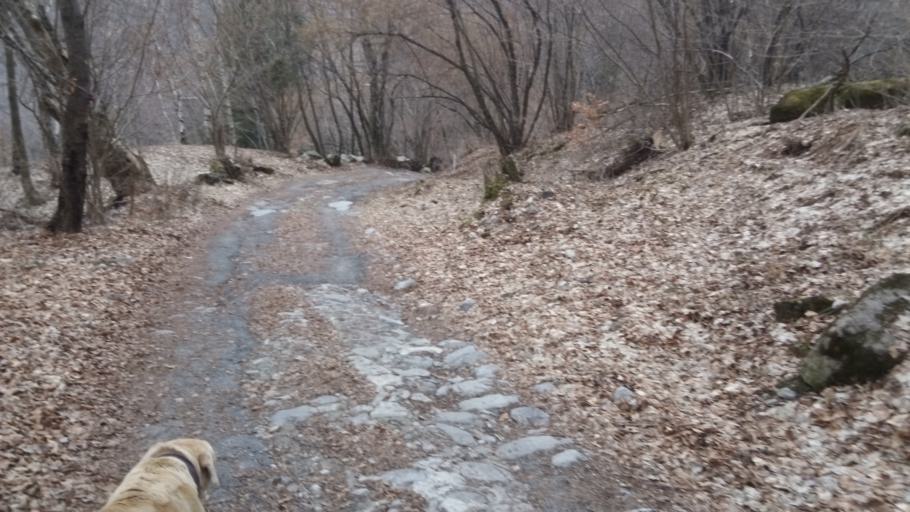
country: IT
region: Lombardy
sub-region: Provincia di Como
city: Occagno
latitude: 45.9128
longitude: 9.1009
